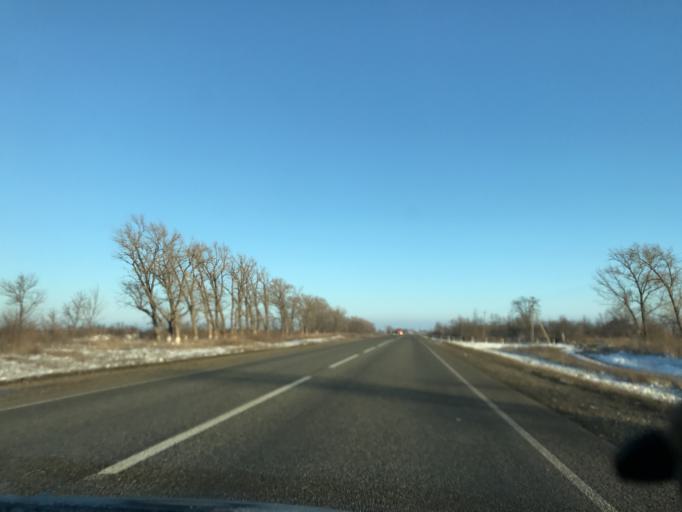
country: RU
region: Stavropol'skiy
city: Bezopasnoye
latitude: 45.6027
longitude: 41.9416
